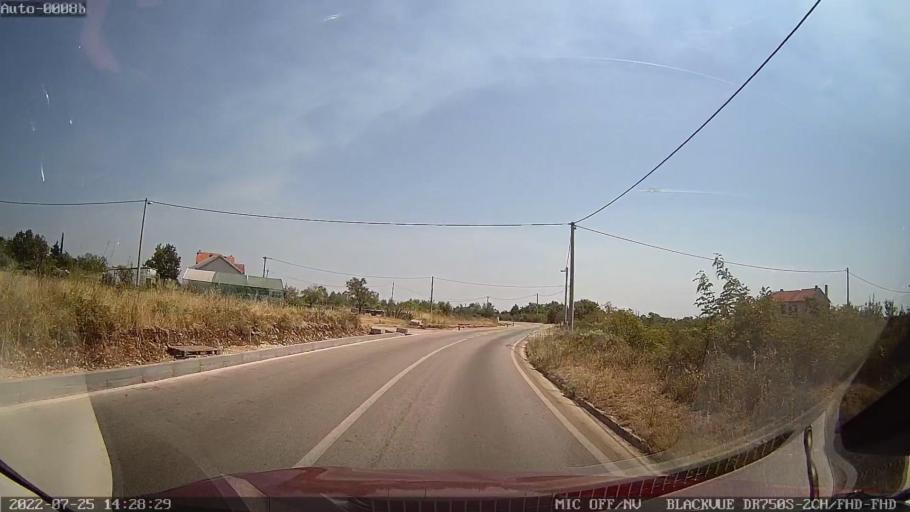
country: HR
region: Zadarska
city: Policnik
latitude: 44.1257
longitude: 15.3489
